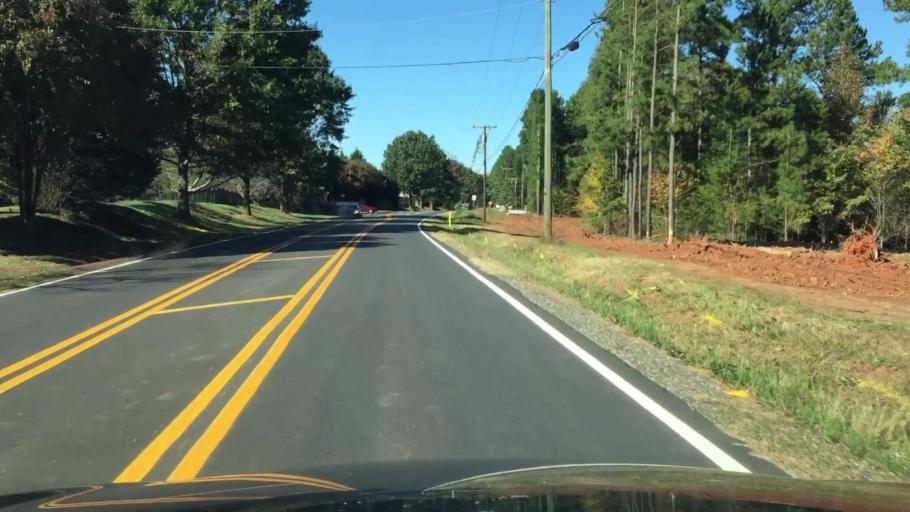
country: US
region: North Carolina
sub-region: Iredell County
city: Mooresville
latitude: 35.5820
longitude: -80.7831
